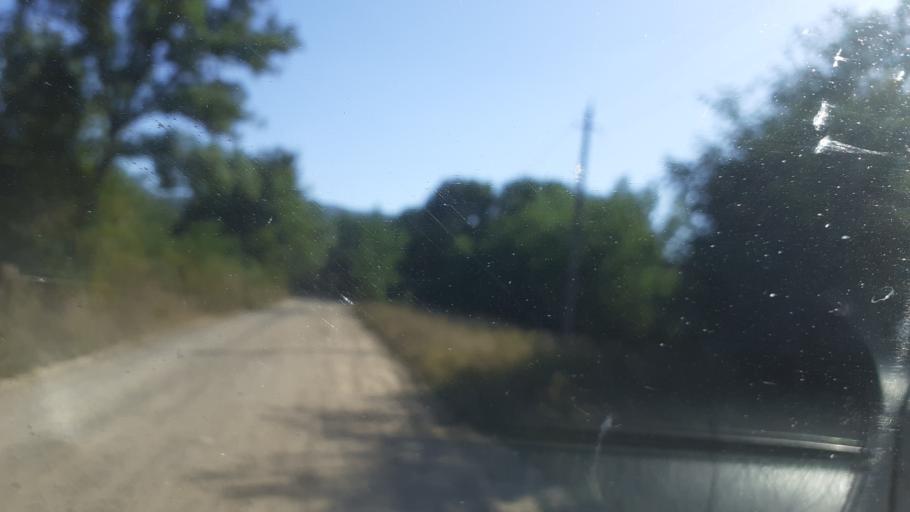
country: RU
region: Krasnodarskiy
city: Azovskaya
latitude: 44.7168
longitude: 38.5271
